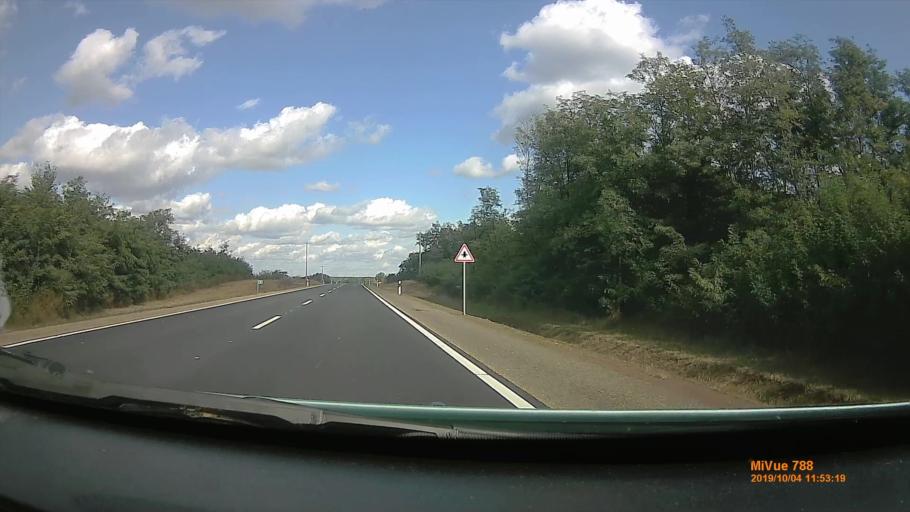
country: HU
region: Szabolcs-Szatmar-Bereg
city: Nyirtelek
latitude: 48.0083
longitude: 21.6755
